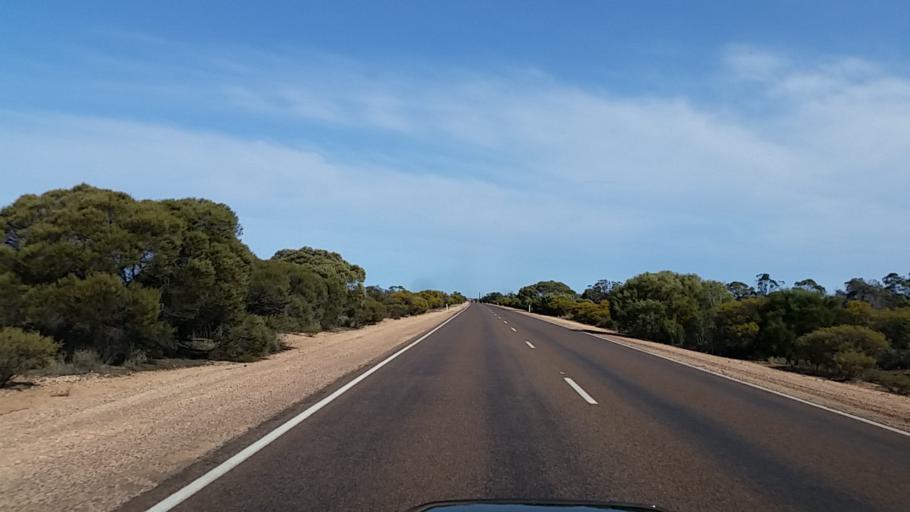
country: AU
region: South Australia
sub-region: Whyalla
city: Whyalla
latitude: -32.9530
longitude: 137.5750
